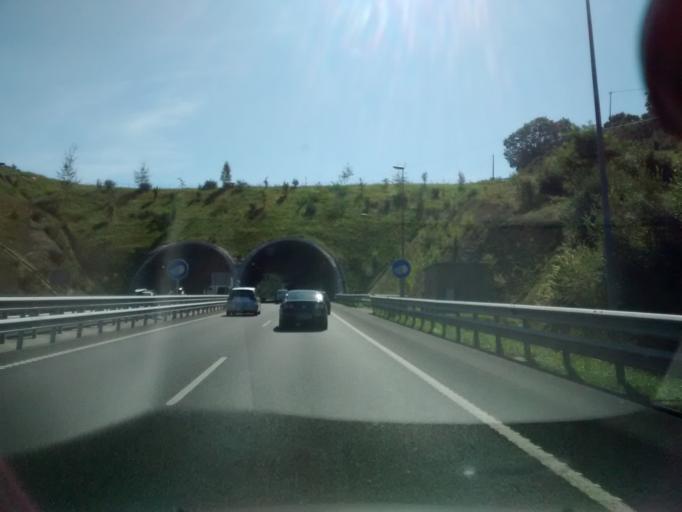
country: ES
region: Basque Country
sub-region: Provincia de Guipuzcoa
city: Hernani
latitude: 43.2772
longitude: -1.9729
